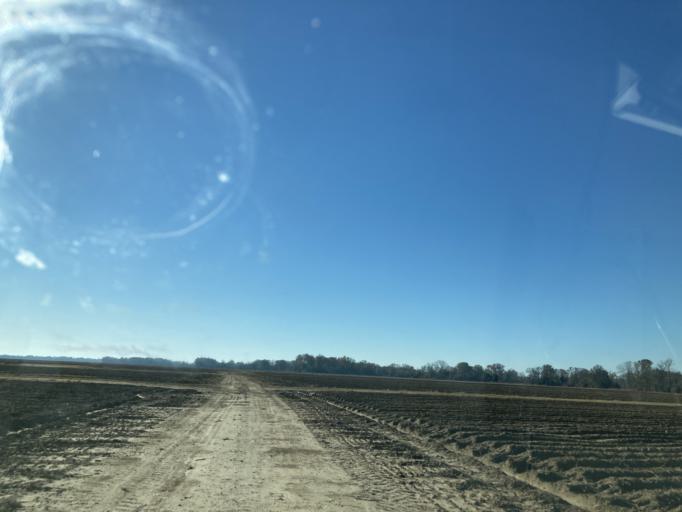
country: US
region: Mississippi
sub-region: Sharkey County
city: Rolling Fork
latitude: 32.8610
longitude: -90.6936
